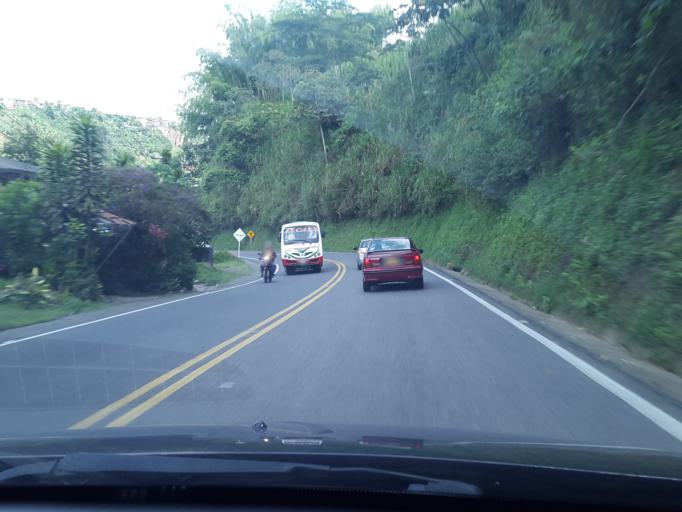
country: CO
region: Risaralda
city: Pereira
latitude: 4.7831
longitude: -75.6954
